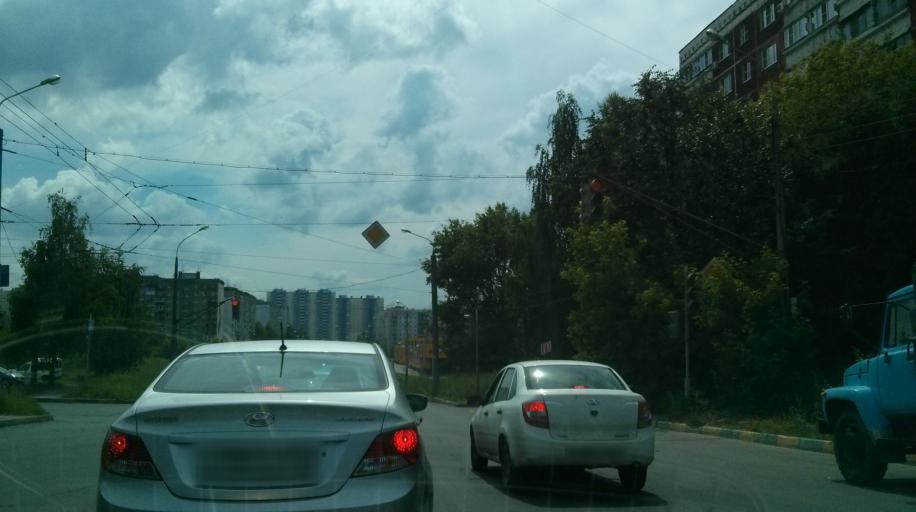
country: RU
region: Nizjnij Novgorod
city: Afonino
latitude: 56.2921
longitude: 44.0681
